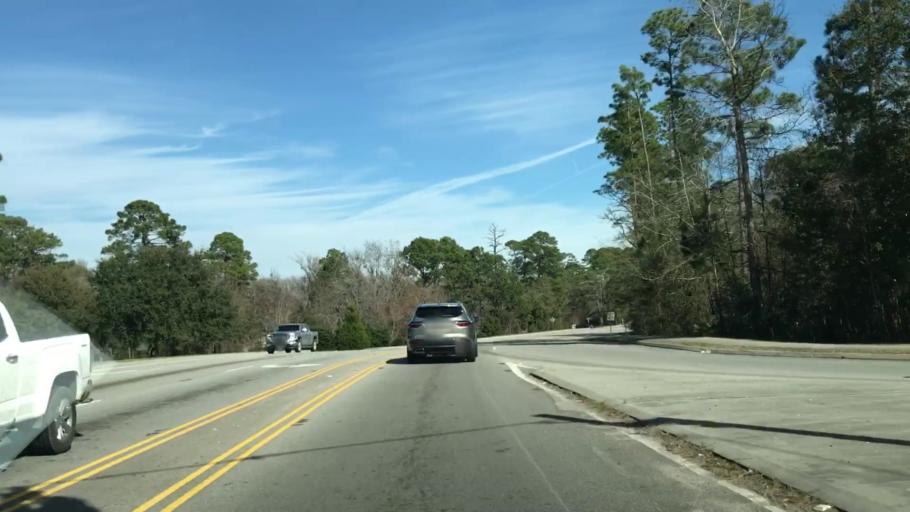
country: US
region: South Carolina
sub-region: Beaufort County
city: Bluffton
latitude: 32.2622
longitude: -80.8707
